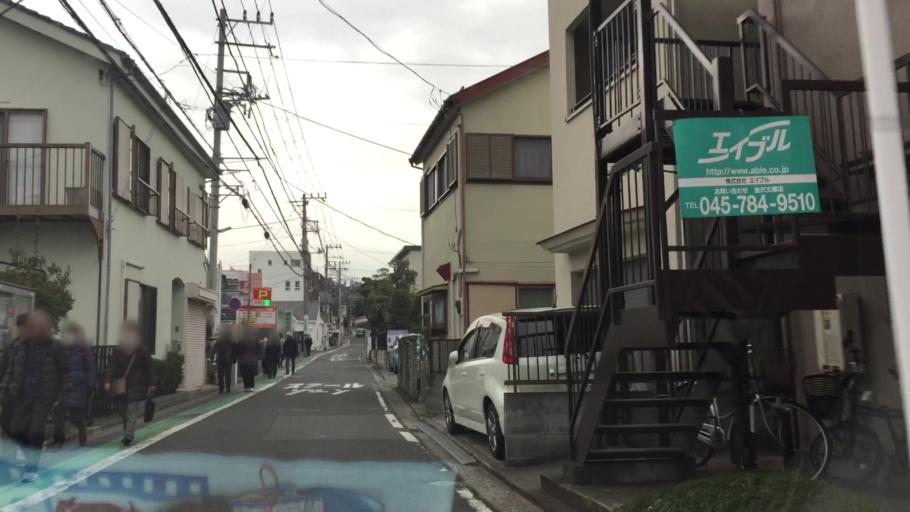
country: JP
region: Kanagawa
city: Yokosuka
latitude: 35.3393
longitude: 139.6281
